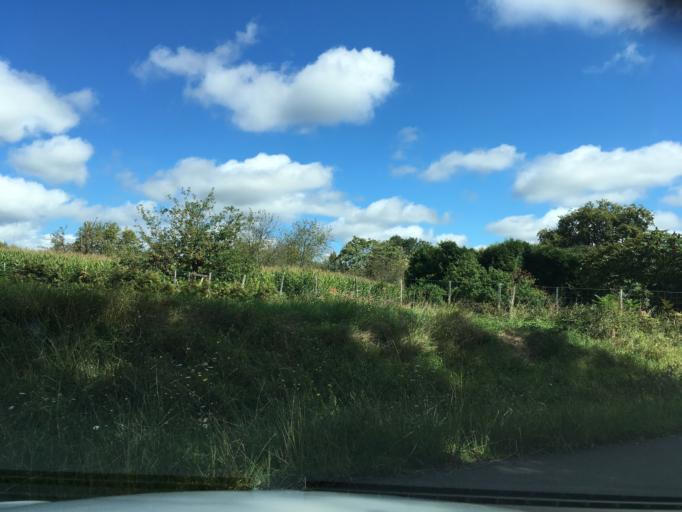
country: FR
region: Aquitaine
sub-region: Departement des Pyrenees-Atlantiques
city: Boucau
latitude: 43.5059
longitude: -1.4563
